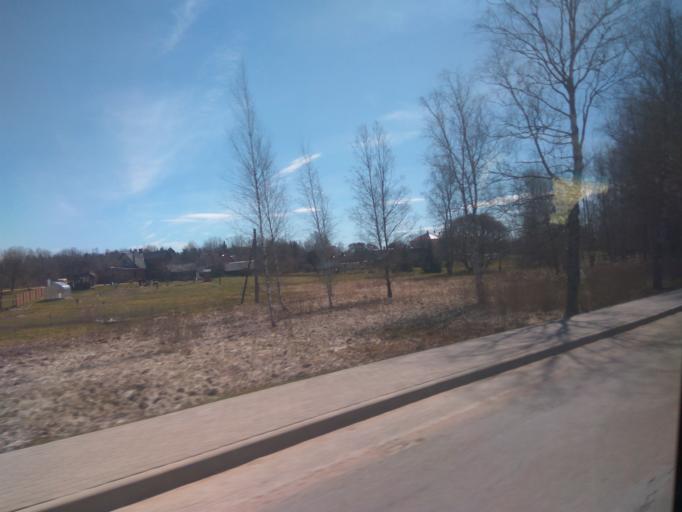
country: LV
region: Aluksnes Rajons
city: Aluksne
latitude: 57.4355
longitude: 27.0386
